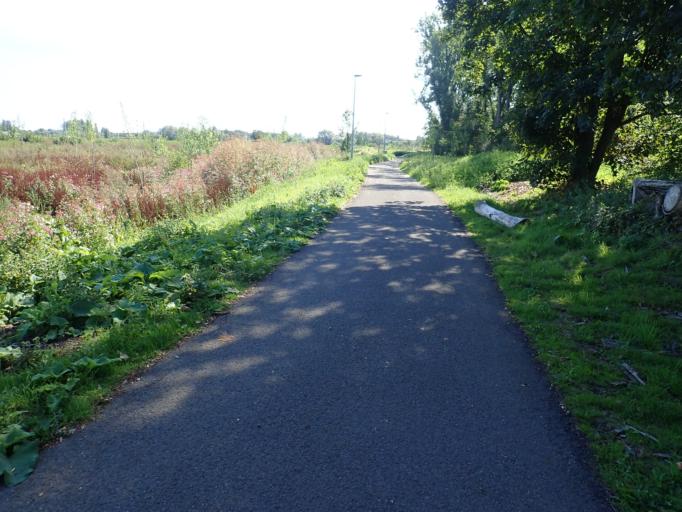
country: BE
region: Flanders
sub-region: Provincie Antwerpen
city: Willebroek
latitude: 51.0698
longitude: 4.3361
